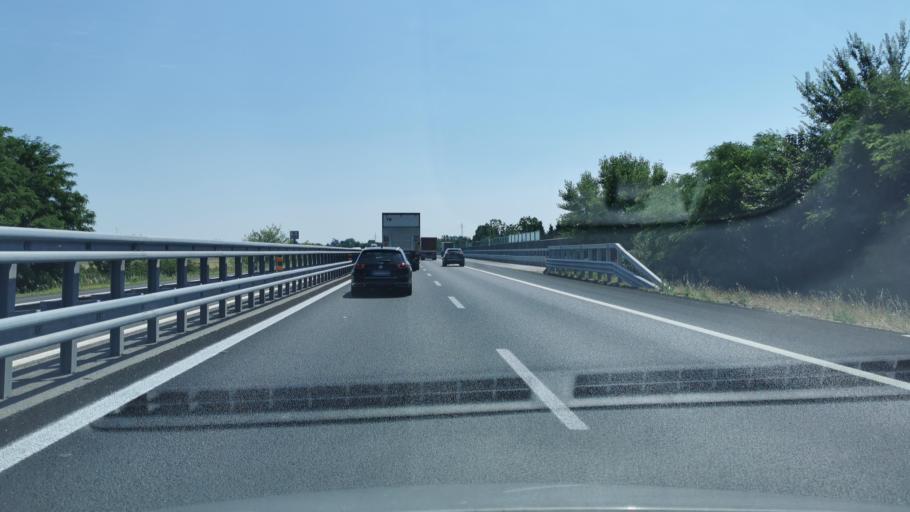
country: IT
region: Emilia-Romagna
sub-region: Provincia di Piacenza
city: San Nicolo
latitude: 45.0639
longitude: 9.5961
